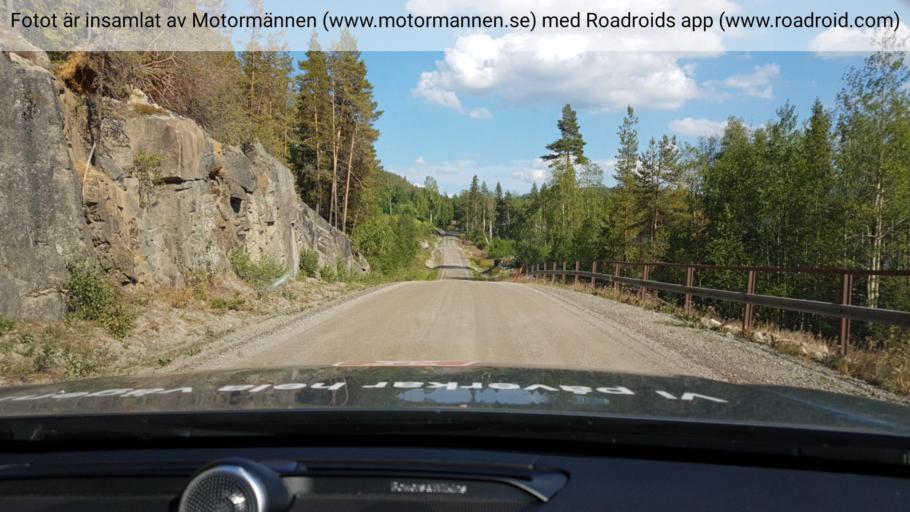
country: SE
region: Jaemtland
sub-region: Stroemsunds Kommun
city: Stroemsund
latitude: 63.9932
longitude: 15.9839
